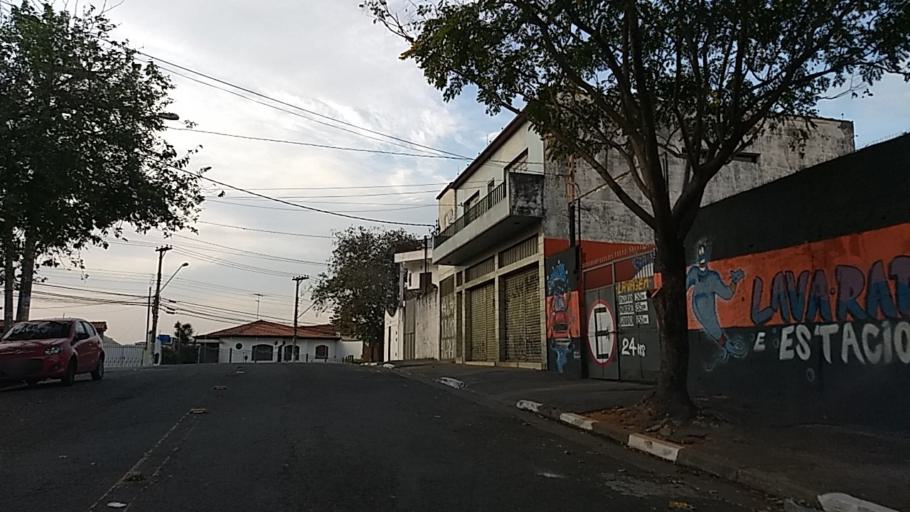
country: BR
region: Sao Paulo
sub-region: Guarulhos
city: Guarulhos
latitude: -23.5033
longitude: -46.5803
